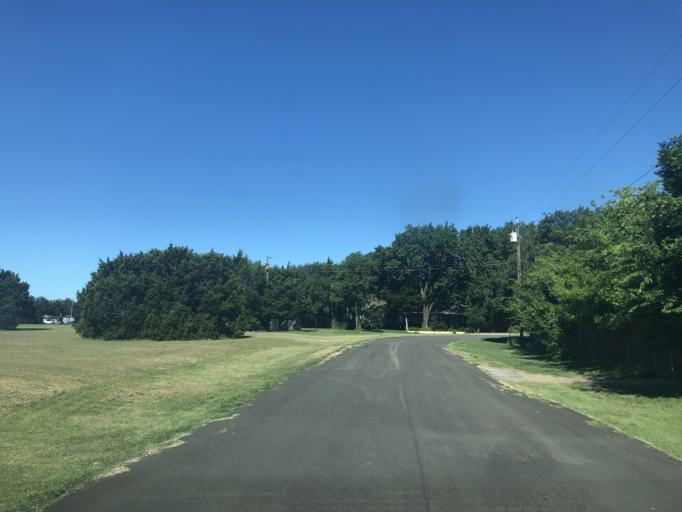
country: US
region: Texas
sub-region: Dallas County
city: Duncanville
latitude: 32.6482
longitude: -96.9399
